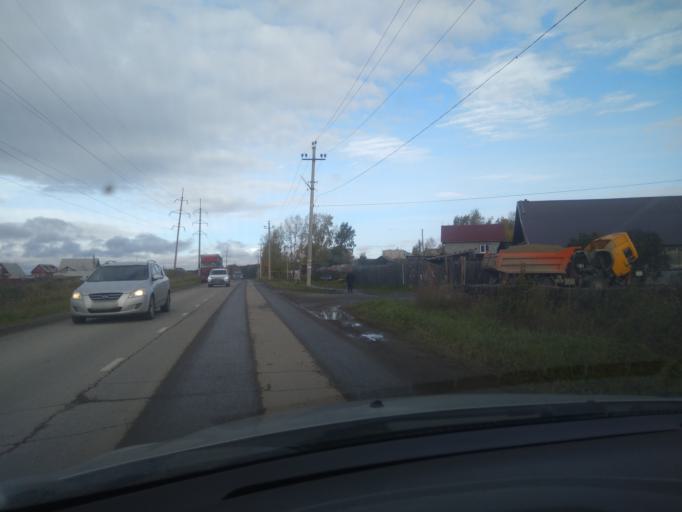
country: RU
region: Sverdlovsk
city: Nikolo-Pavlovskoye
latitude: 57.7960
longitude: 60.0526
